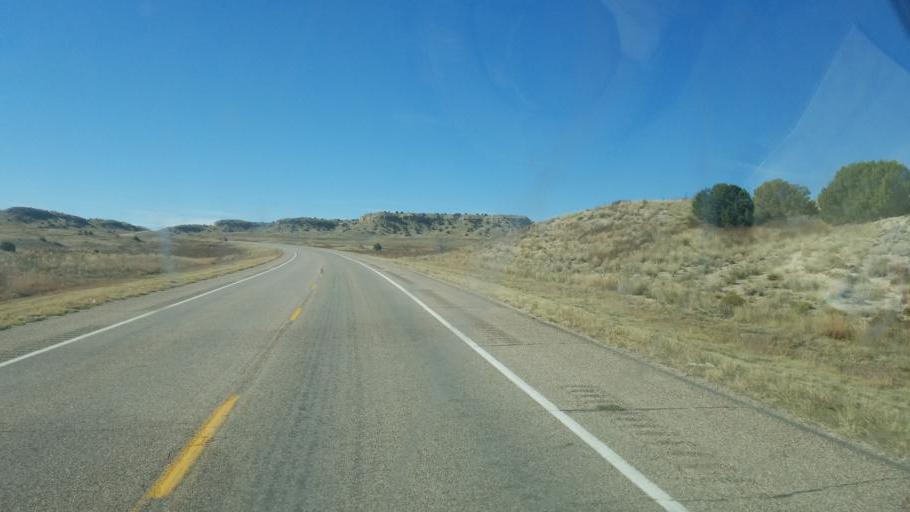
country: US
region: Colorado
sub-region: Pueblo County
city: Pueblo West
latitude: 38.2549
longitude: -104.7186
